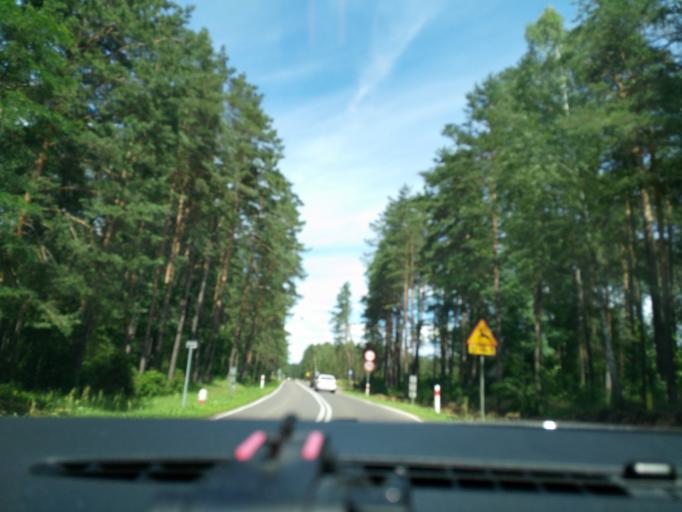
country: PL
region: Podlasie
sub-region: Powiat augustowski
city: Augustow
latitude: 53.8474
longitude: 23.0445
